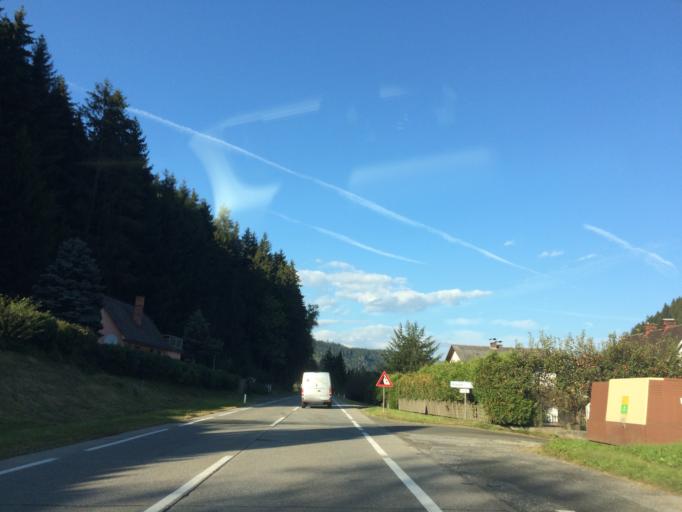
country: AT
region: Styria
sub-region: Politischer Bezirk Leoben
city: Sankt Michael in Obersteiermark
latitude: 47.3421
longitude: 15.0492
